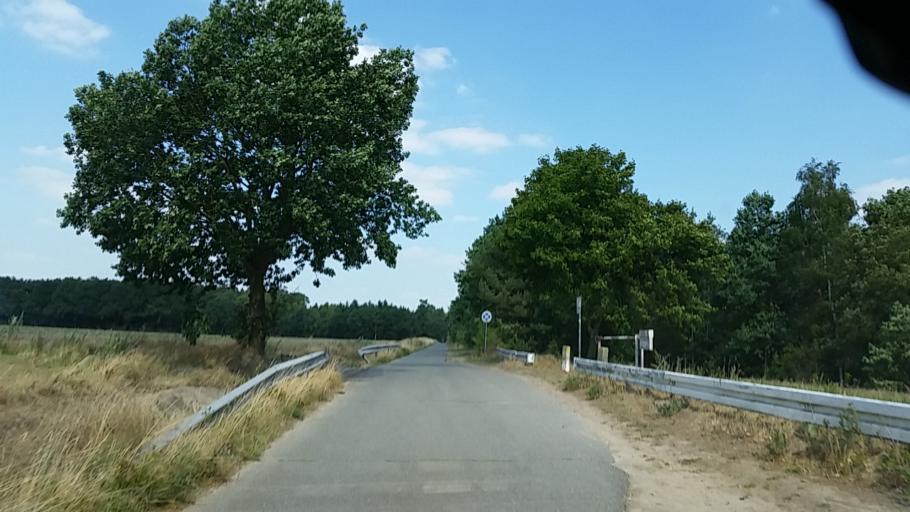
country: DE
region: Lower Saxony
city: Wendisch Evern
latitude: 53.2249
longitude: 10.4903
